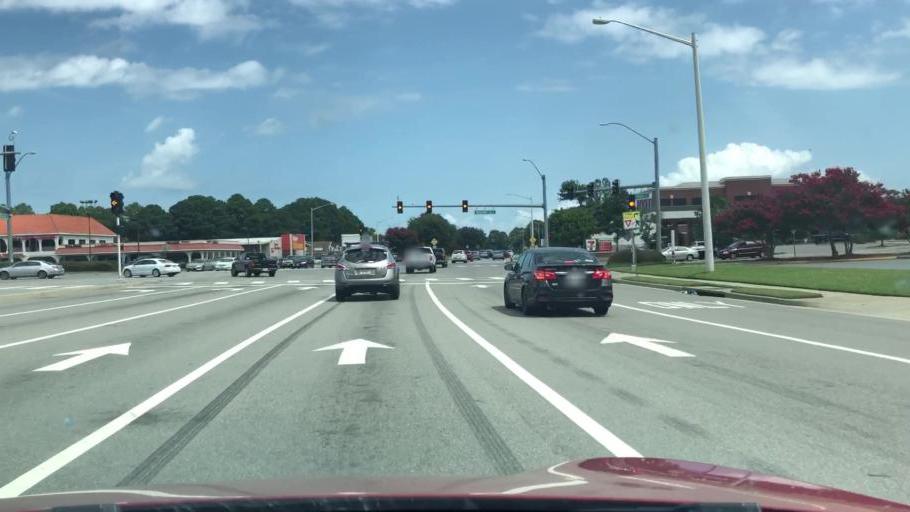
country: US
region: Virginia
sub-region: City of Chesapeake
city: Chesapeake
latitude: 36.8748
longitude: -76.1347
